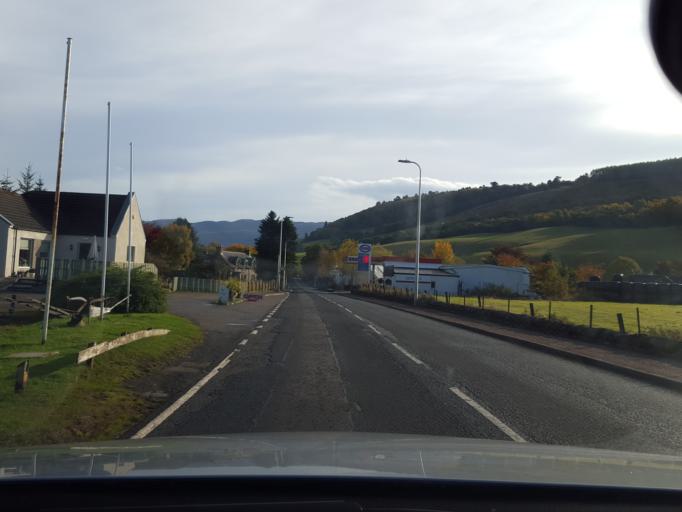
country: GB
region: Scotland
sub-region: Highland
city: Beauly
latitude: 57.3285
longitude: -4.4764
